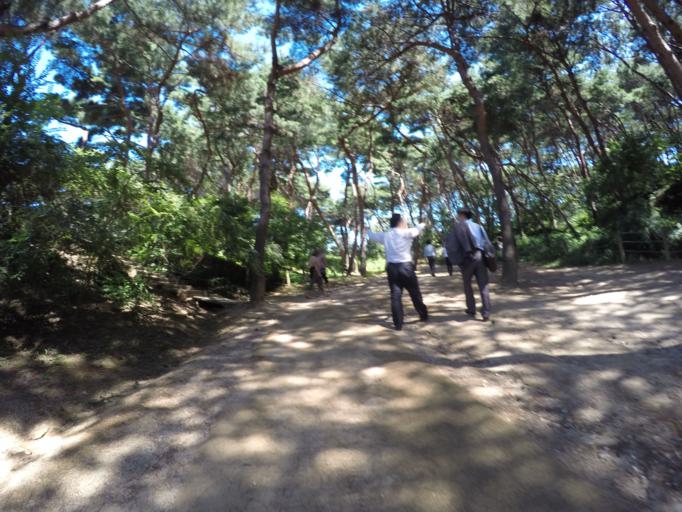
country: KR
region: Seoul
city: Seoul
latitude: 37.5095
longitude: 127.0474
